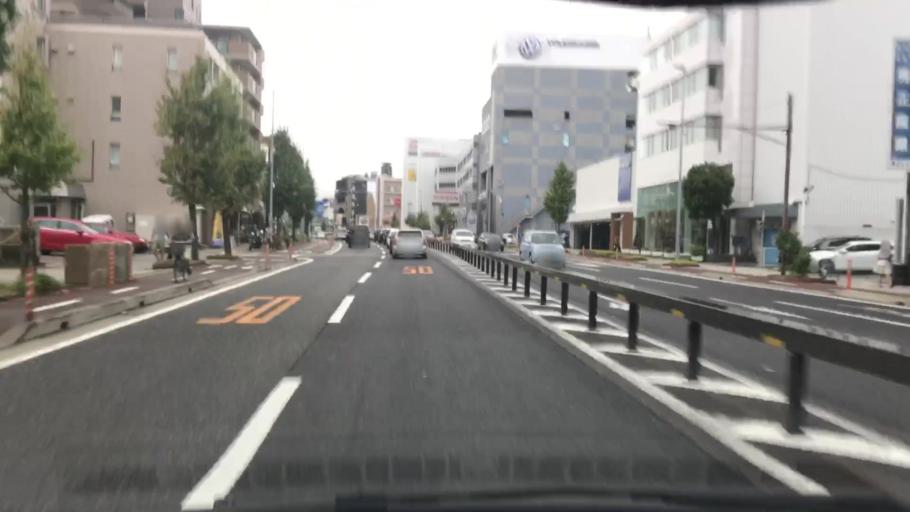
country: JP
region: Hyogo
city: Nishinomiya-hama
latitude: 34.7386
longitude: 135.3357
